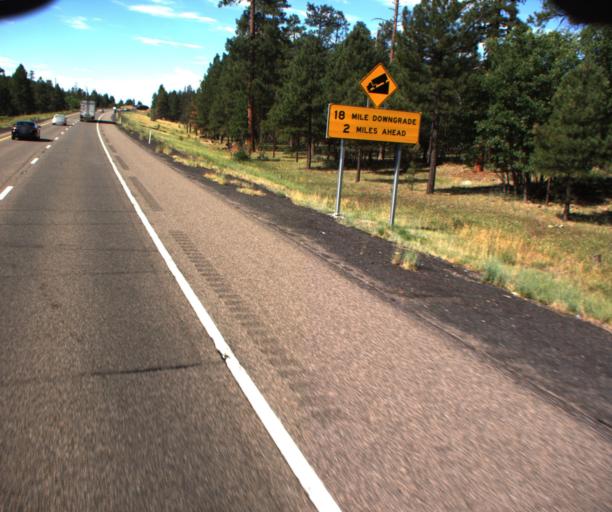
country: US
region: Arizona
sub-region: Coconino County
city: Sedona
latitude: 34.8334
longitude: -111.6061
